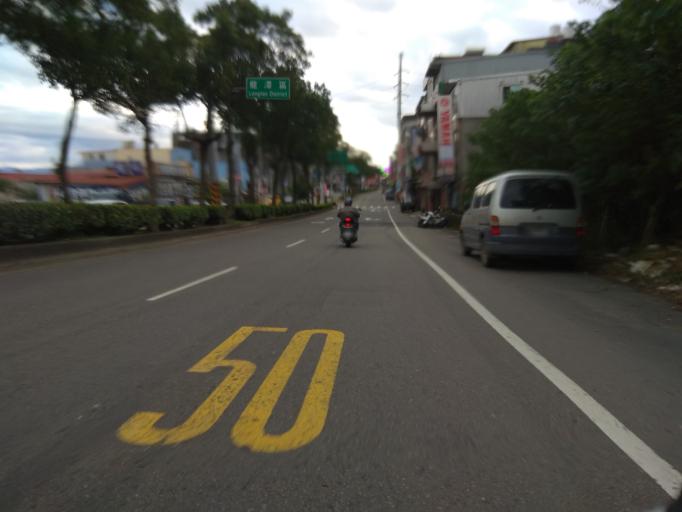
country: TW
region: Taiwan
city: Daxi
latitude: 24.8914
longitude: 121.2123
